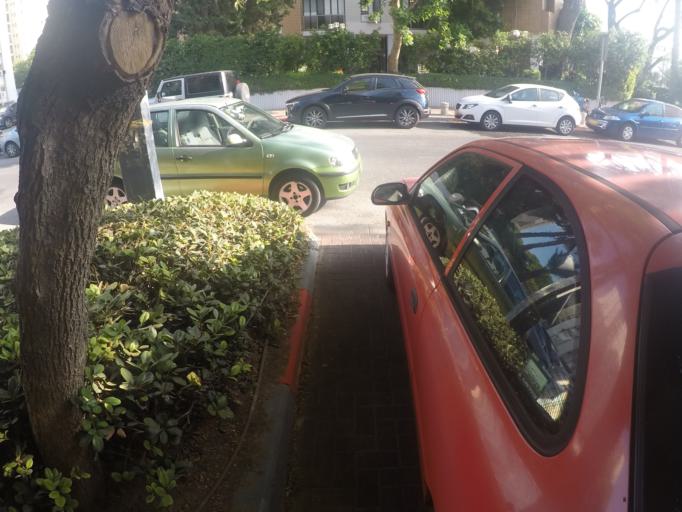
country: IL
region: Tel Aviv
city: Ramat Gan
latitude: 32.1110
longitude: 34.7945
